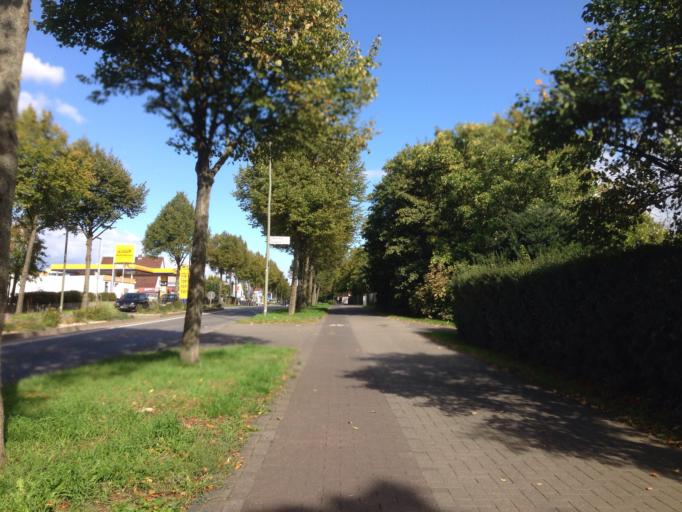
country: DE
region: Hesse
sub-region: Regierungsbezirk Giessen
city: Giessen
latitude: 50.6020
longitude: 8.6895
